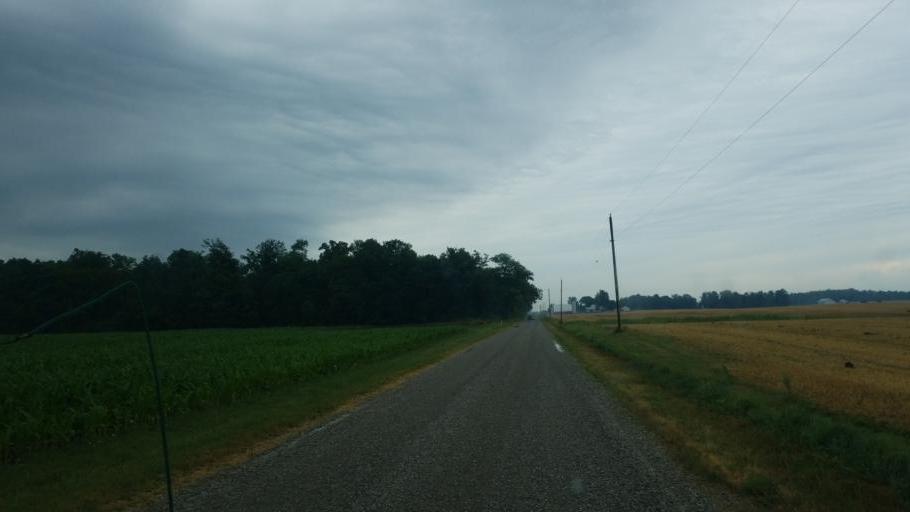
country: US
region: Indiana
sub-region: DeKalb County
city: Butler
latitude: 41.4571
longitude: -84.9100
